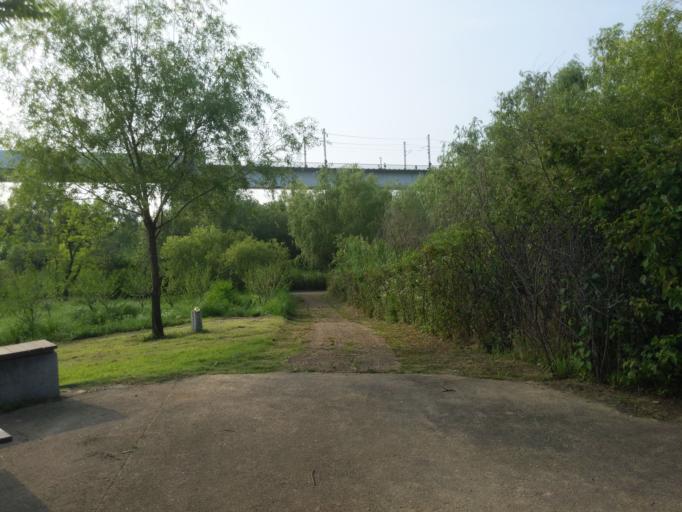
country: KR
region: Gyeonggi-do
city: Kwangmyong
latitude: 37.5367
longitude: 126.9057
